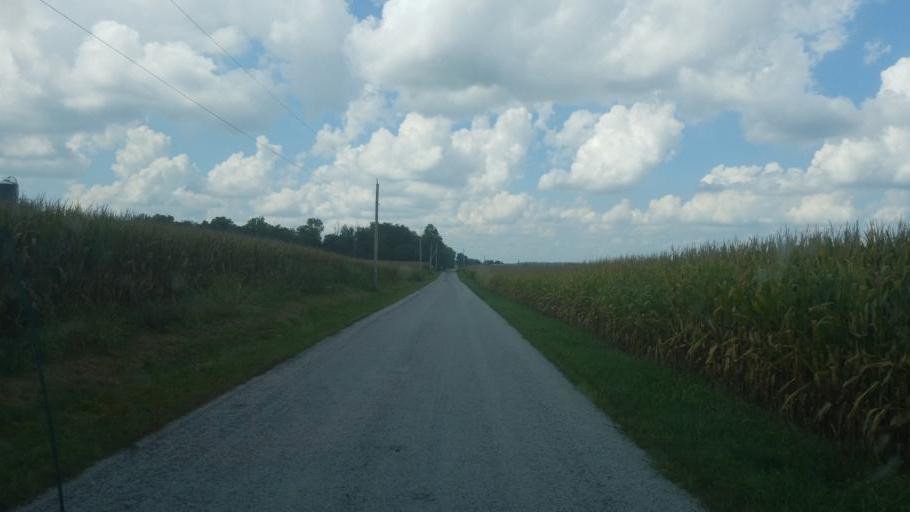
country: US
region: Ohio
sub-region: Hardin County
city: Kenton
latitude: 40.6881
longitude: -83.5698
